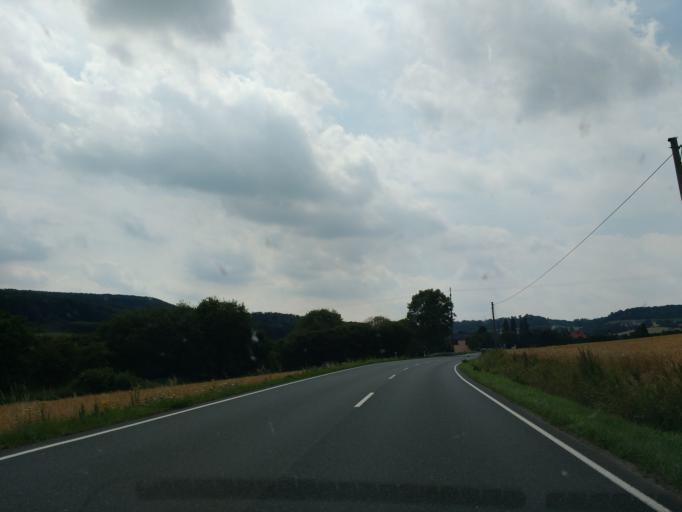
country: DE
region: North Rhine-Westphalia
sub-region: Regierungsbezirk Detmold
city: Barntrup
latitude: 52.0058
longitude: 9.1807
